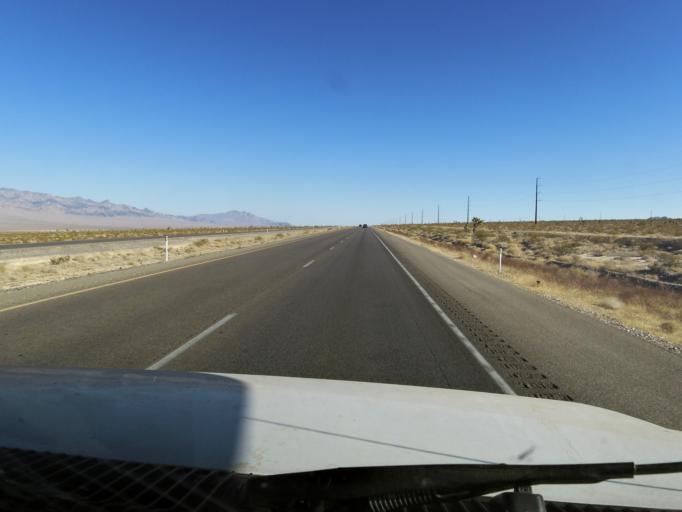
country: US
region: Nevada
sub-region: Clark County
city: Summerlin South
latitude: 36.4958
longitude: -115.5002
